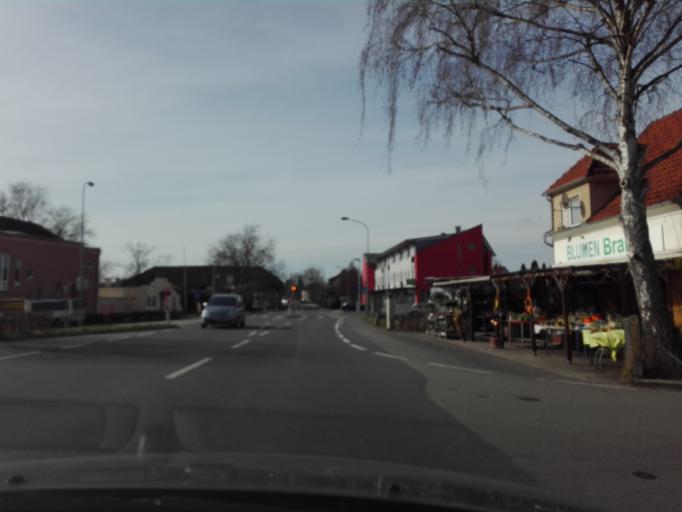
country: AT
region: Upper Austria
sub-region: Politischer Bezirk Linz-Land
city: Ansfelden
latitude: 48.2253
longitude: 14.2961
